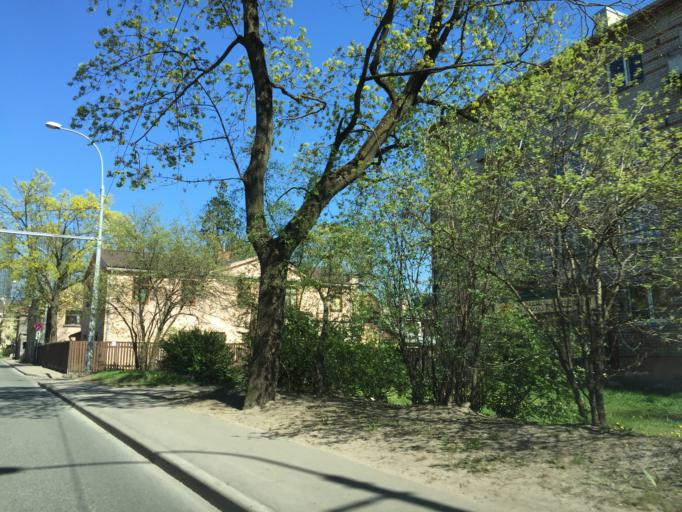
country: LV
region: Riga
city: Riga
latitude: 56.9434
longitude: 24.0723
